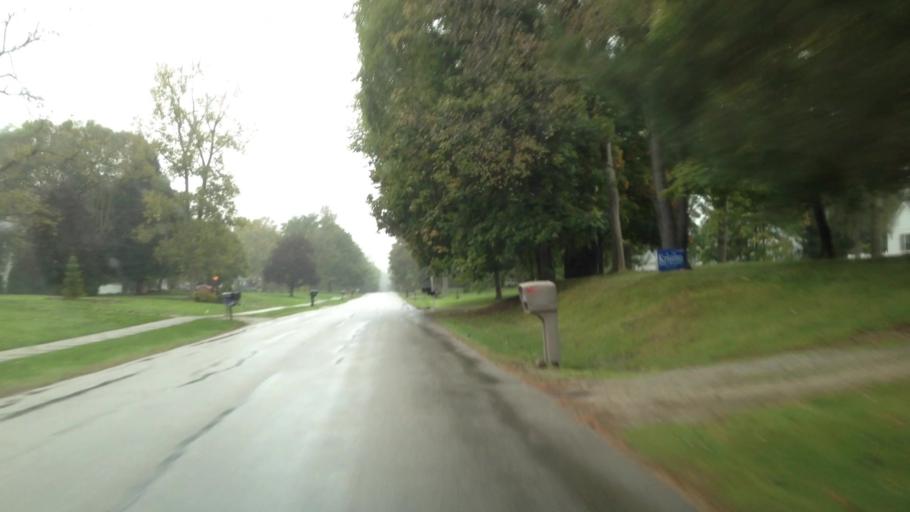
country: US
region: Ohio
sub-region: Summit County
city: Hudson
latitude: 41.2547
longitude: -81.4210
